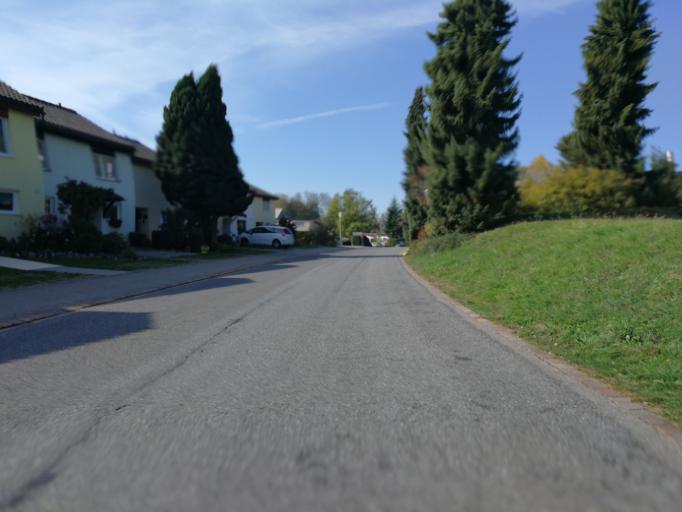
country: CH
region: Zurich
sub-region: Bezirk Hinwil
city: Rueti / Oberdorf
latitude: 47.2759
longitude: 8.8740
